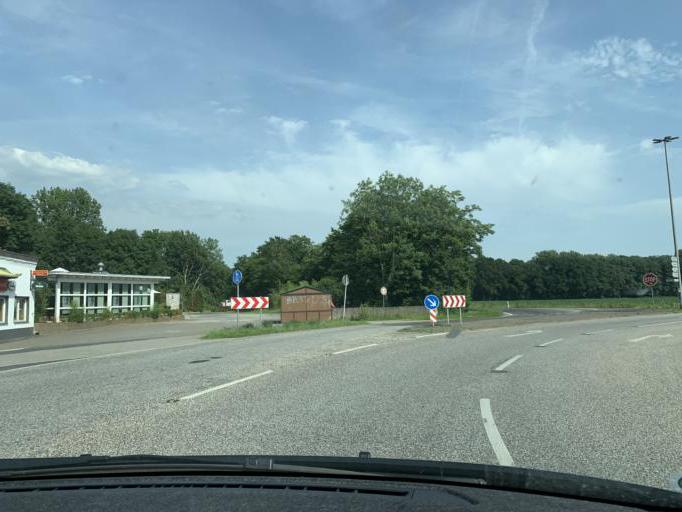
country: DE
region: North Rhine-Westphalia
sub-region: Regierungsbezirk Dusseldorf
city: Viersen
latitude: 51.2637
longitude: 6.4155
